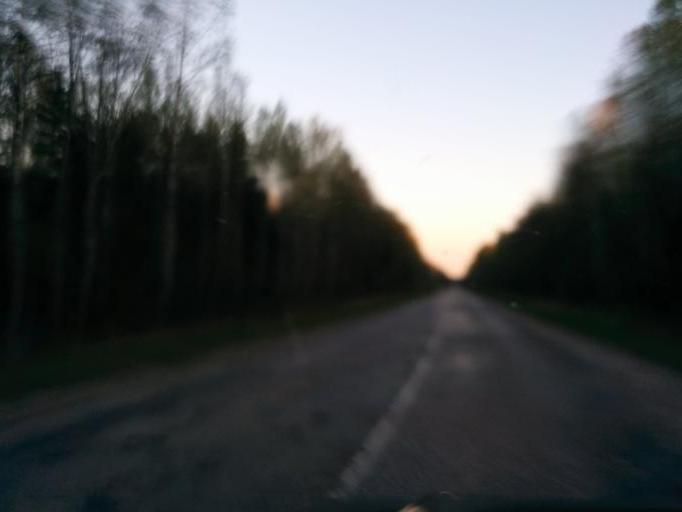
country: LV
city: Tireli
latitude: 56.8564
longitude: 23.5360
